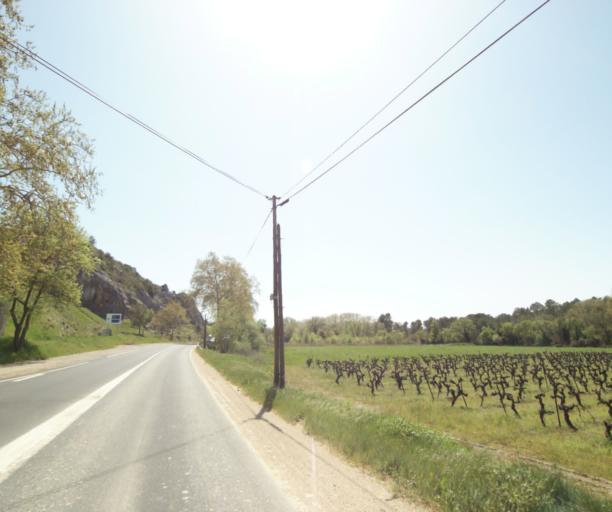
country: FR
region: Languedoc-Roussillon
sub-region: Departement de l'Herault
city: Prades-le-Lez
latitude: 43.7087
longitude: 3.8678
